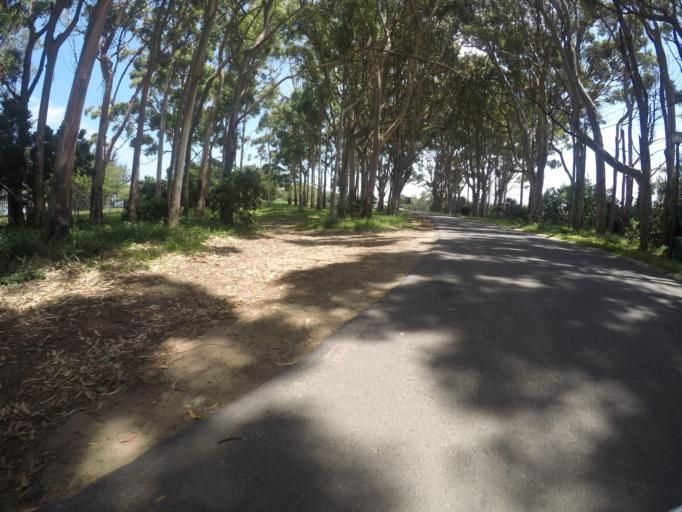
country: ZA
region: Eastern Cape
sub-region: Buffalo City Metropolitan Municipality
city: East London
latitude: -32.9956
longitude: 27.9327
